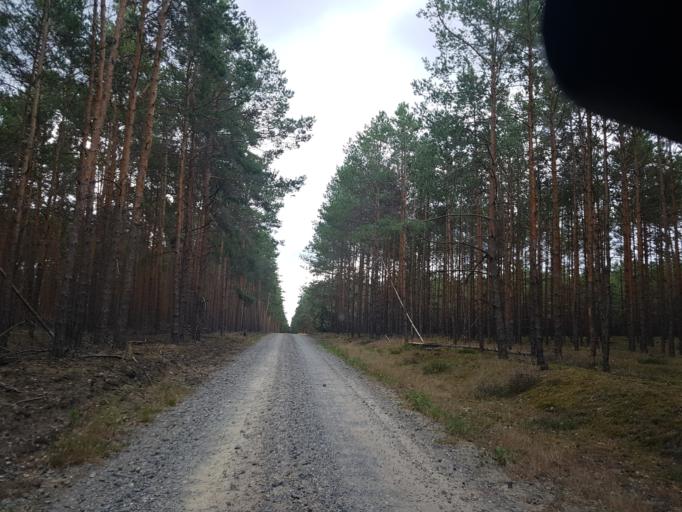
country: DE
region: Brandenburg
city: Sallgast
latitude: 51.6270
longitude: 13.8021
